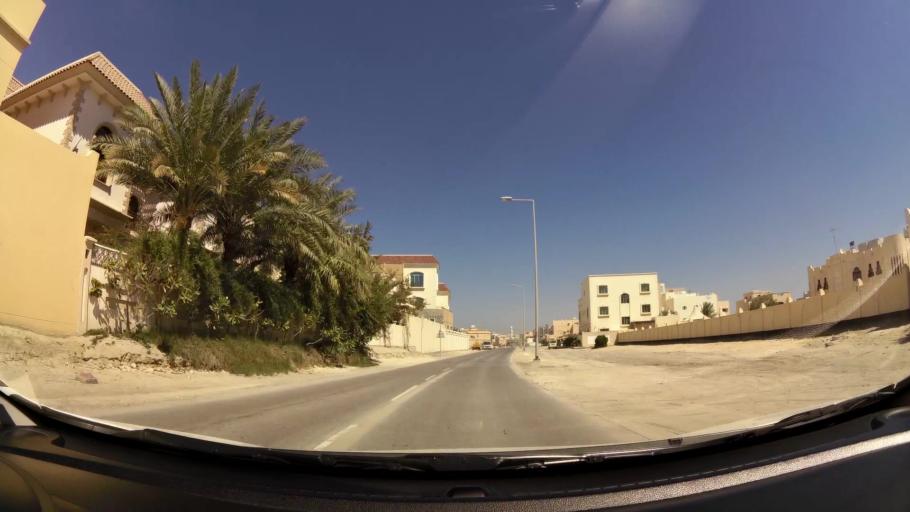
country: BH
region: Muharraq
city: Al Muharraq
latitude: 26.2688
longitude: 50.6013
